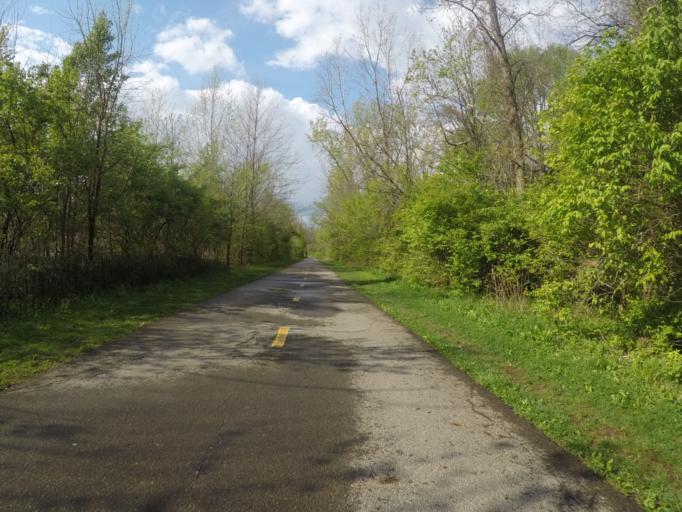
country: US
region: Ohio
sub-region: Franklin County
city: Grandview Heights
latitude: 40.0188
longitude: -83.0172
